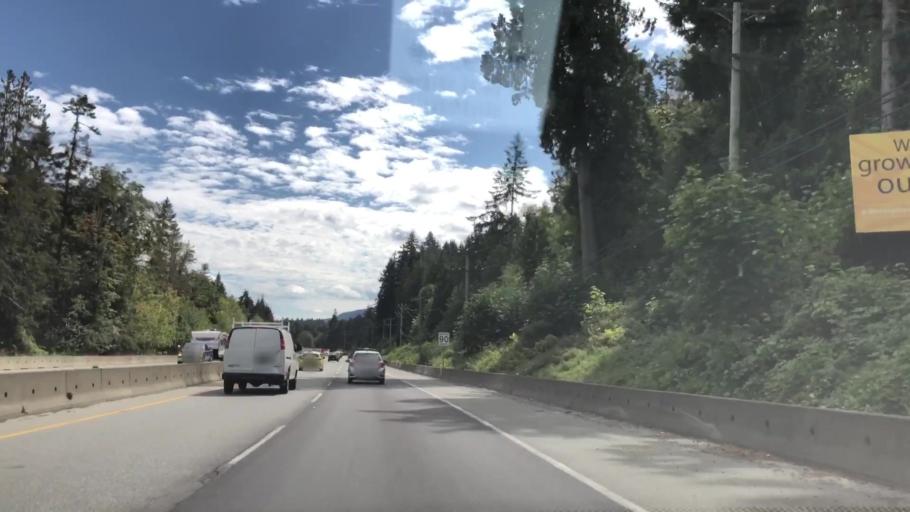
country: CA
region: British Columbia
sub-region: Cowichan Valley Regional District
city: Ladysmith
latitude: 49.0204
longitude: -123.8602
